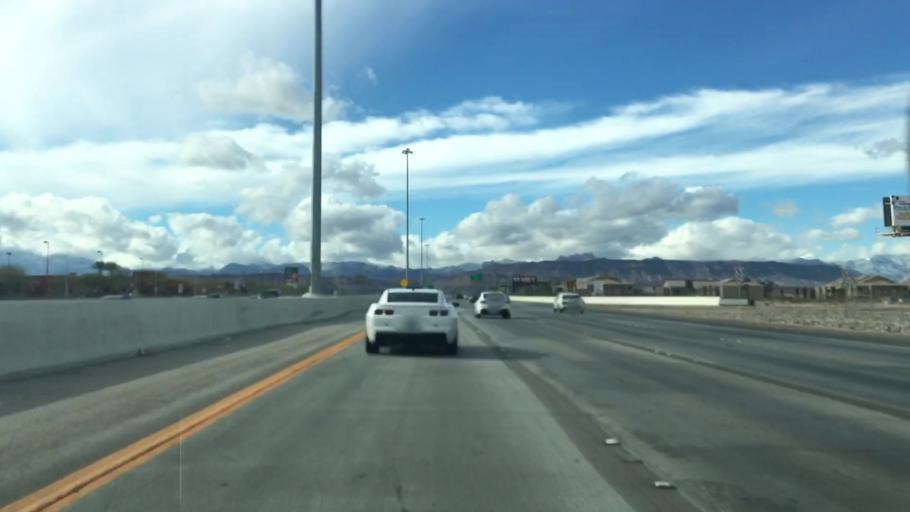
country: US
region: Nevada
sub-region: Clark County
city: Spring Valley
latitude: 36.0666
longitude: -115.2445
